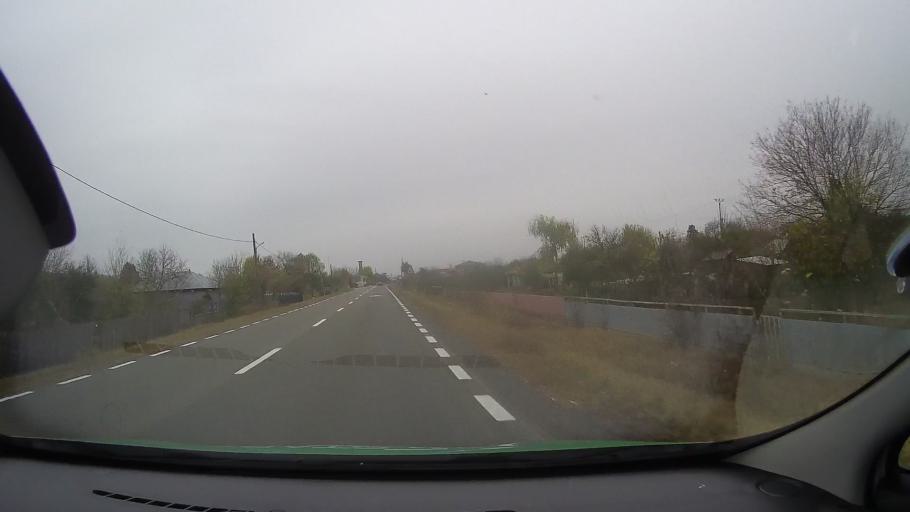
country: RO
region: Ialomita
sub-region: Comuna Giurgeni
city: Giurgeni
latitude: 44.7464
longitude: 27.8569
